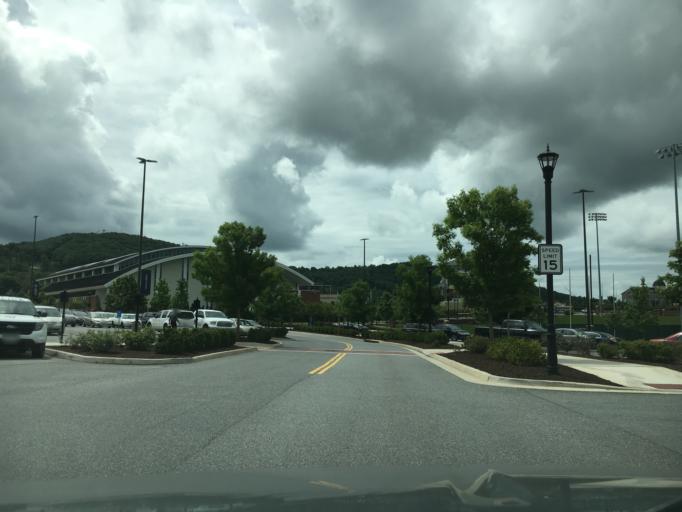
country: US
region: Virginia
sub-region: City of Lynchburg
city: West Lynchburg
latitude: 37.3577
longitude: -79.1762
